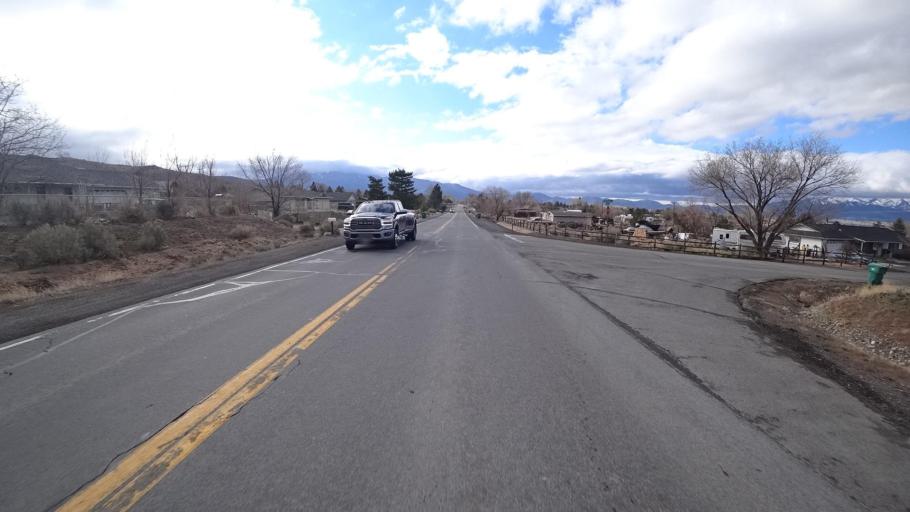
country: US
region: Nevada
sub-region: Storey County
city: Virginia City
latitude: 39.3071
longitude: -119.7872
